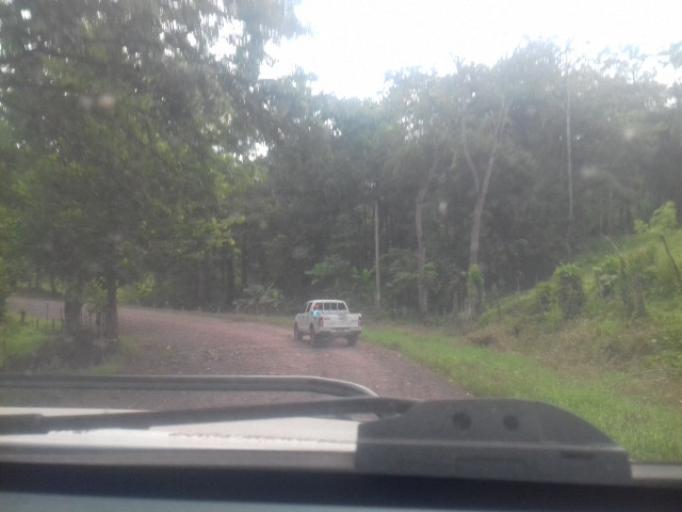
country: NI
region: Atlantico Norte (RAAN)
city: Waslala
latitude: 13.4260
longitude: -85.3137
